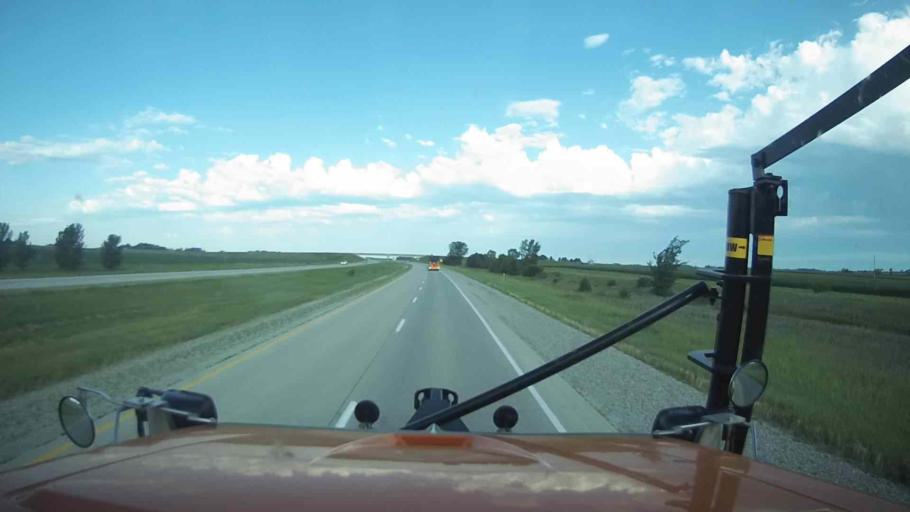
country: US
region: Iowa
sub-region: Cerro Gordo County
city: Clear Lake
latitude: 43.1055
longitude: -93.3133
